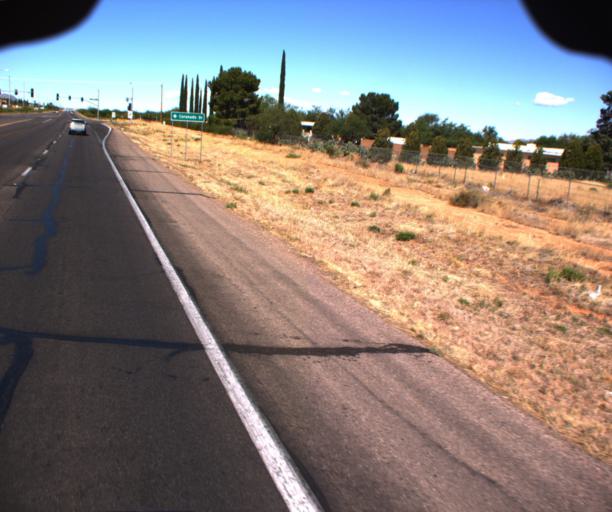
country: US
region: Arizona
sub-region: Cochise County
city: Sierra Vista
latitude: 31.5695
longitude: -110.2724
